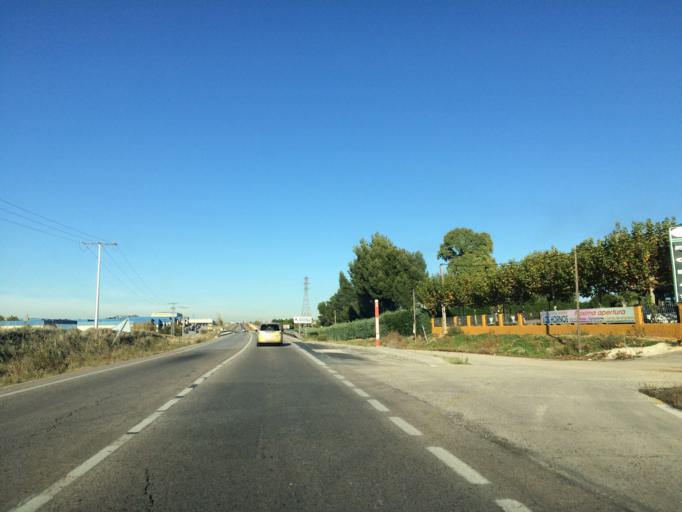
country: ES
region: Madrid
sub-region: Provincia de Madrid
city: Serranillos del Valle
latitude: 40.1931
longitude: -3.8757
